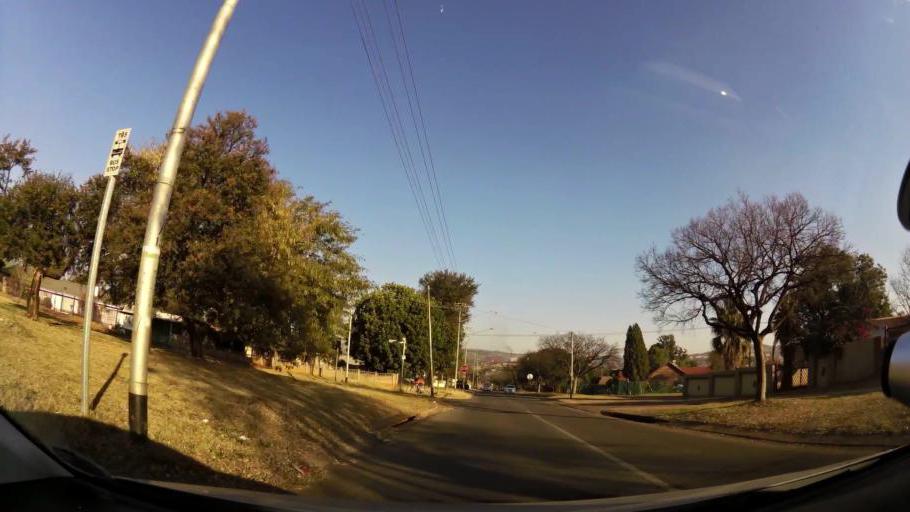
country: ZA
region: Gauteng
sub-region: City of Tshwane Metropolitan Municipality
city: Pretoria
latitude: -25.7381
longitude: 28.1243
